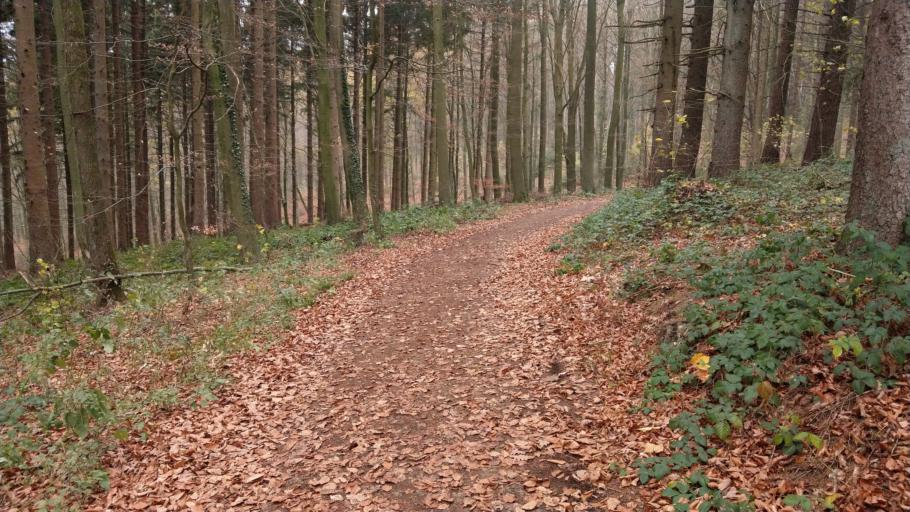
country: NL
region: Limburg
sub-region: Gemeente Vaals
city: Vaals
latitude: 50.7458
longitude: 6.0531
